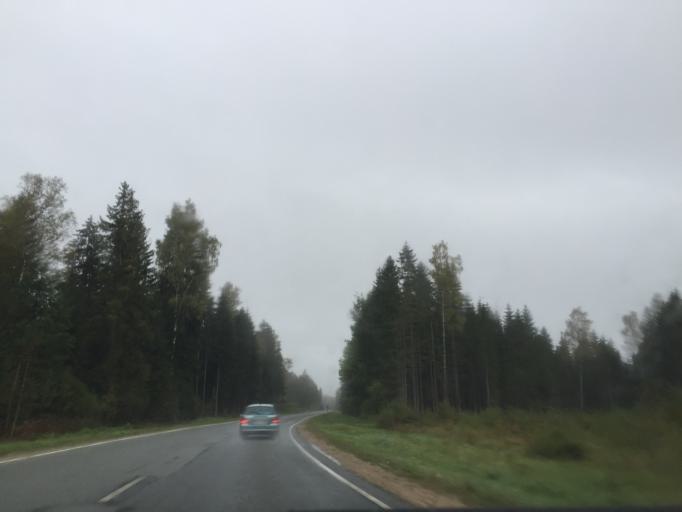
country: LV
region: Incukalns
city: Incukalns
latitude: 57.0554
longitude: 24.6724
